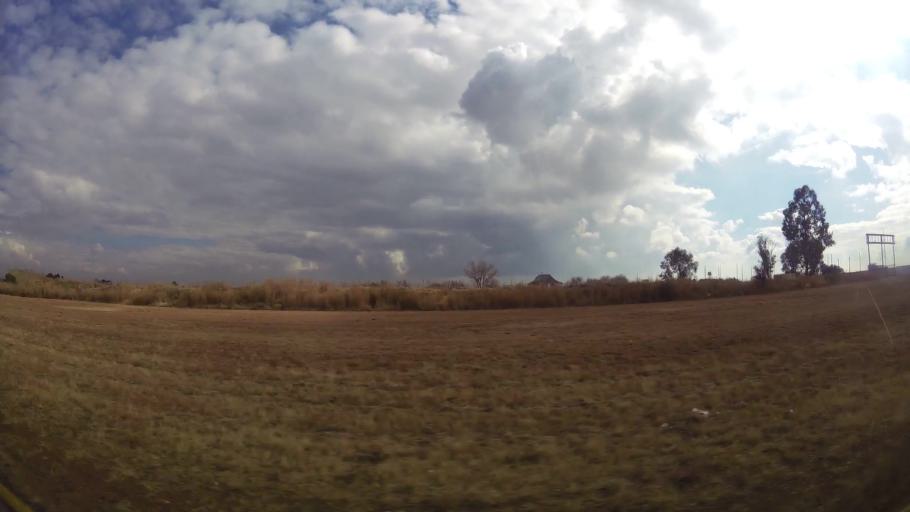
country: ZA
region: Gauteng
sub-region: Sedibeng District Municipality
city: Meyerton
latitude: -26.6165
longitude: 28.0609
